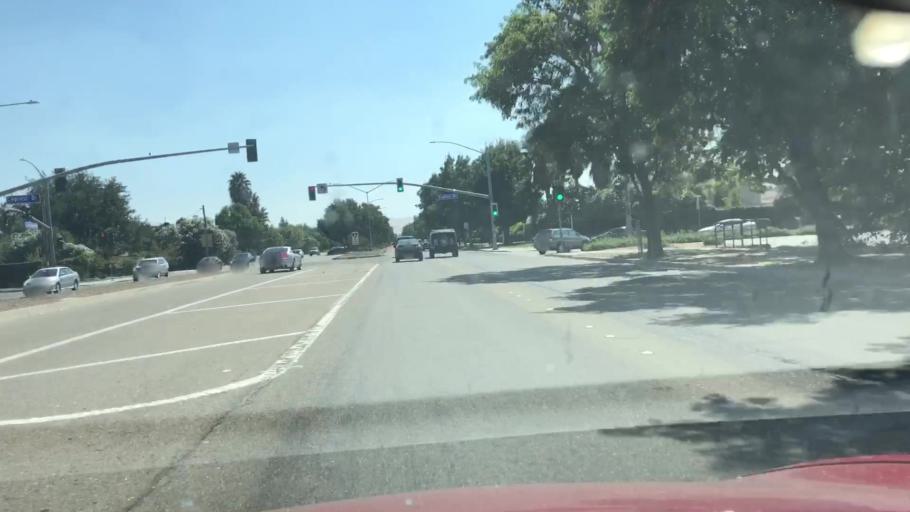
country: US
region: California
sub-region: San Joaquin County
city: Tracy
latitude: 37.7356
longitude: -121.4532
